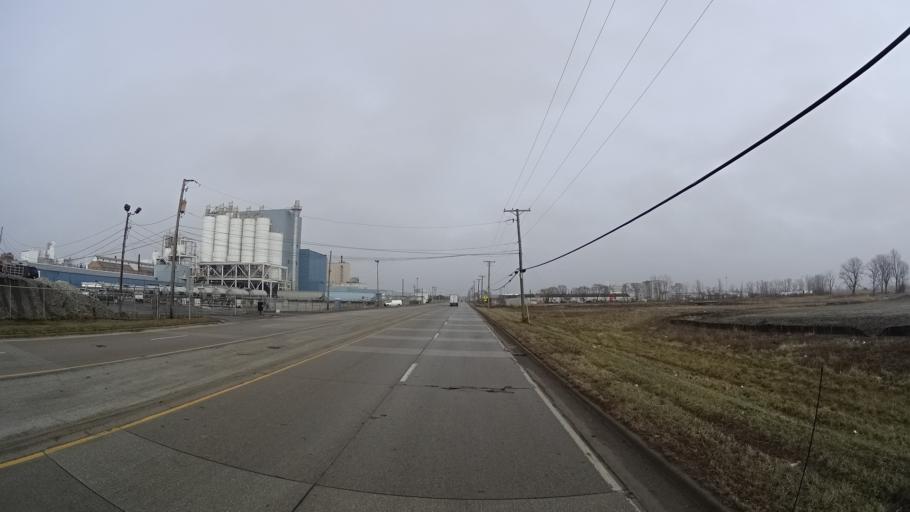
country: US
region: Illinois
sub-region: Cook County
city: Chicago Heights
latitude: 41.5102
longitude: -87.6161
